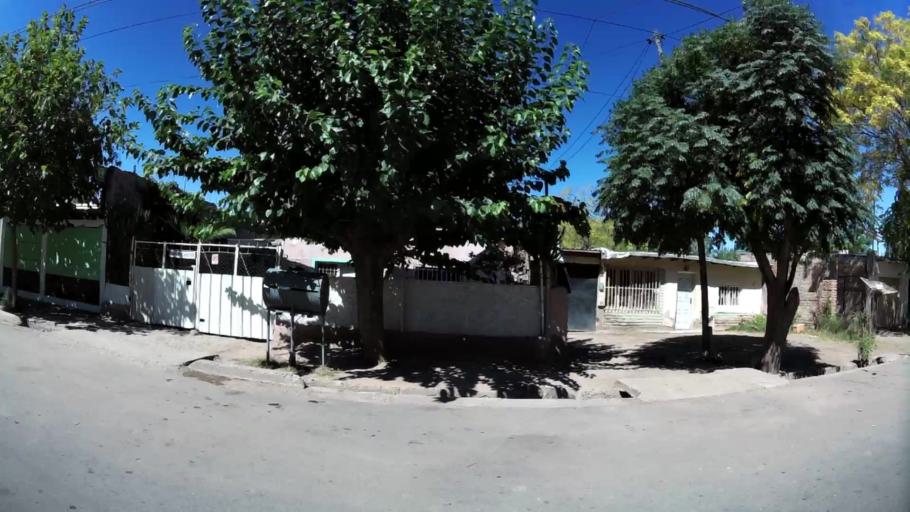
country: AR
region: Mendoza
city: Las Heras
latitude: -32.8270
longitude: -68.8243
